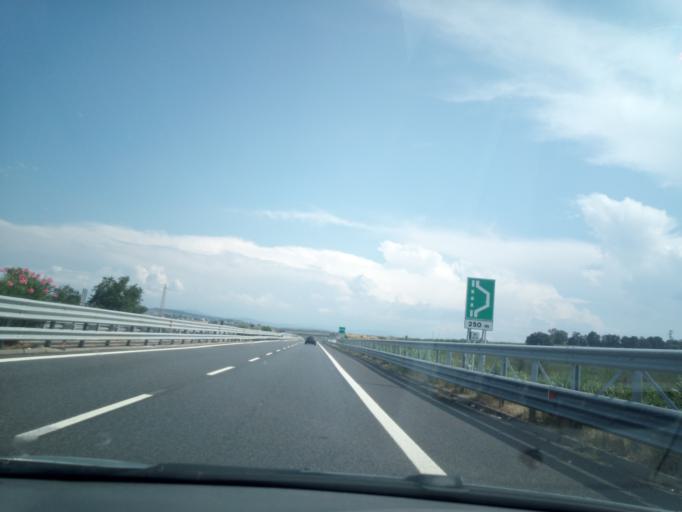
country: IT
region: Calabria
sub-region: Provincia di Cosenza
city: Firmo
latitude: 39.7200
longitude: 16.2398
